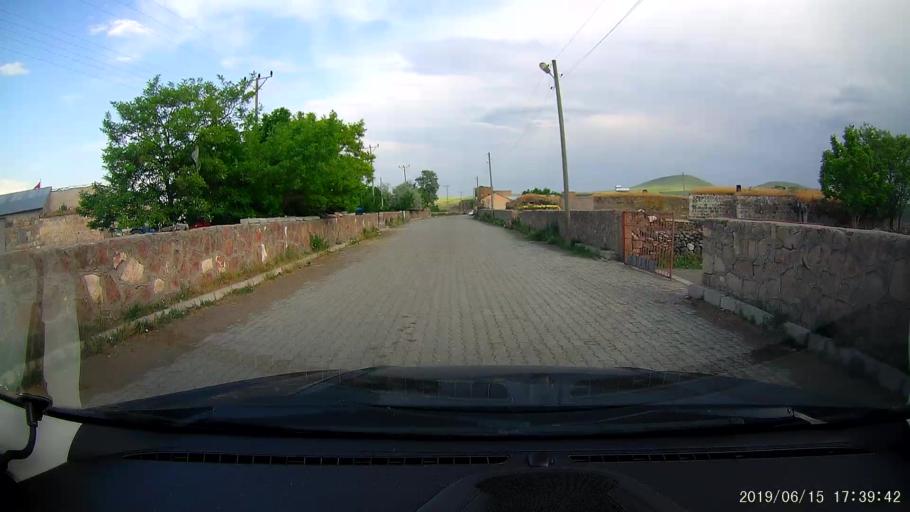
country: TR
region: Kars
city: Basgedikler
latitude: 40.5148
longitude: 43.5708
